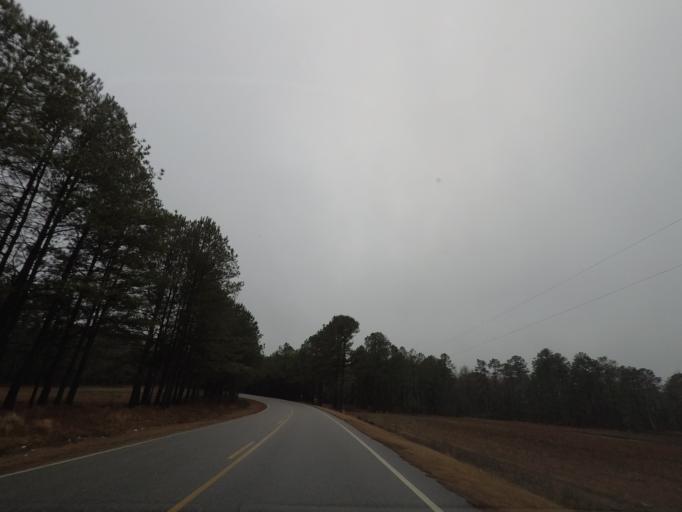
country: US
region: North Carolina
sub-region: Cumberland County
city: Spring Lake
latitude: 35.2678
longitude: -78.9948
